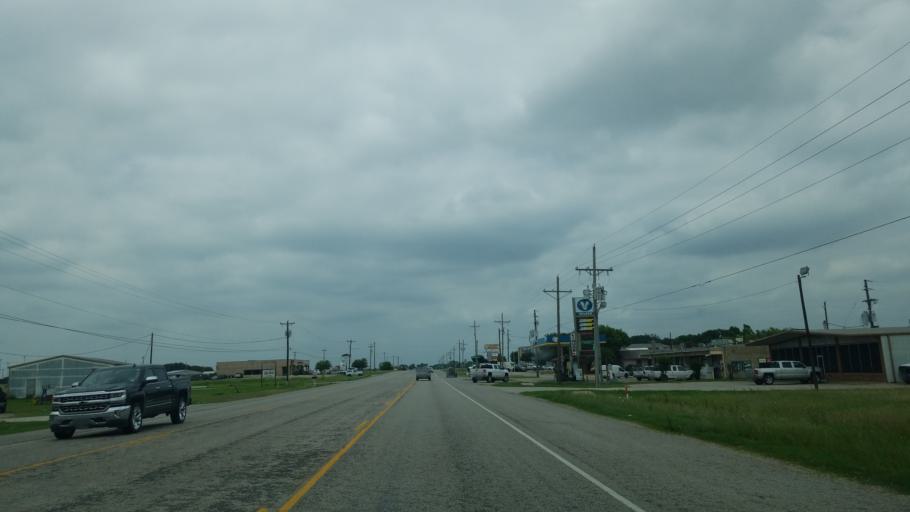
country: US
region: Texas
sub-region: Denton County
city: Pilot Point
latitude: 33.4072
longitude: -96.9424
